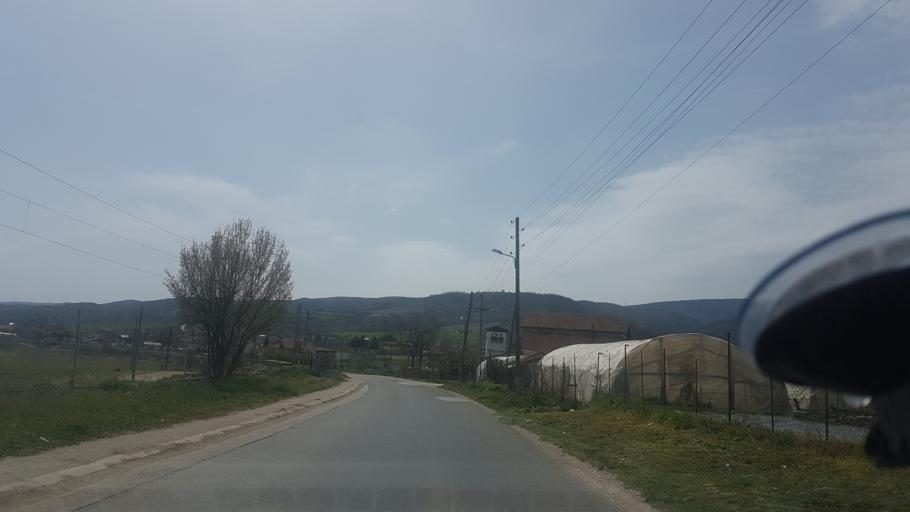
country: MK
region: Zelenikovo
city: Zelenikovo
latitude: 41.8870
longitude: 21.5878
